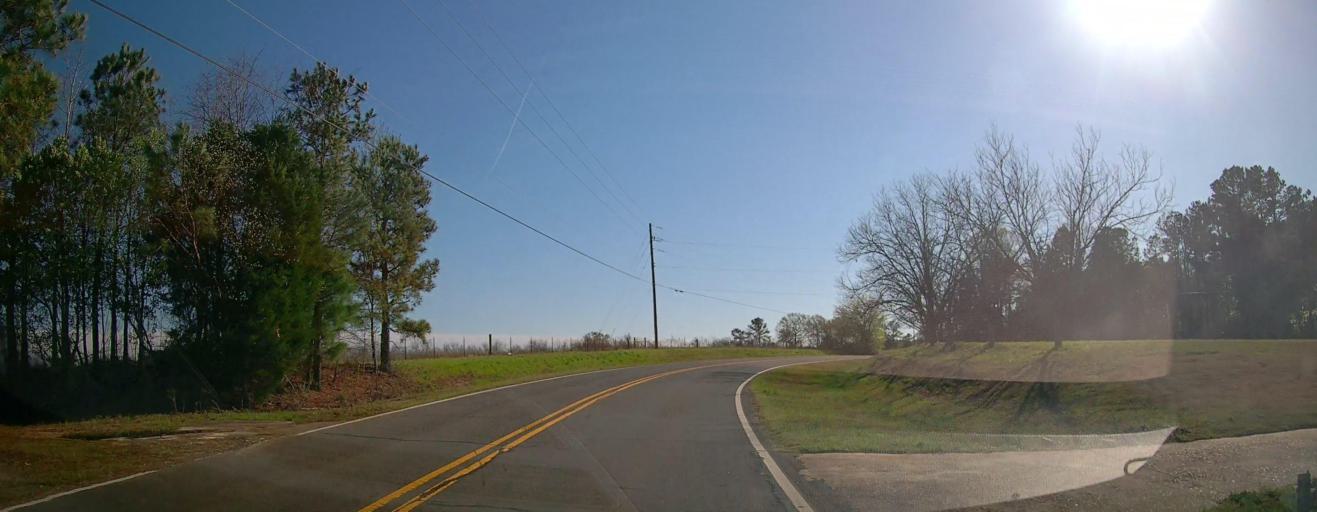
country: US
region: Georgia
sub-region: Peach County
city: Fort Valley
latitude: 32.5125
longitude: -83.9198
